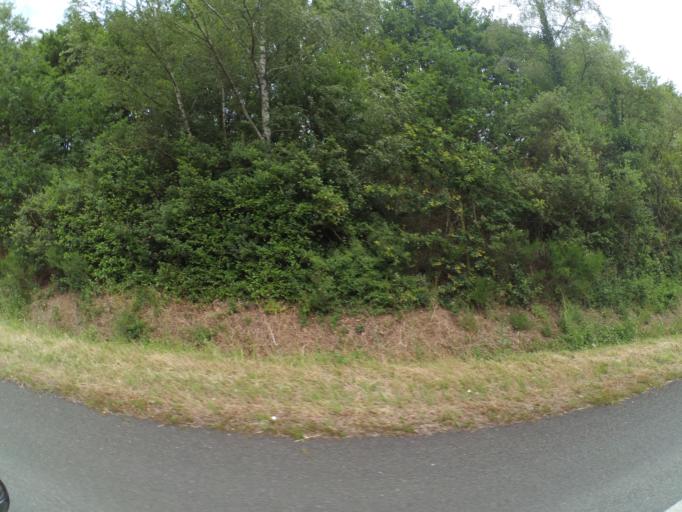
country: FR
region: Pays de la Loire
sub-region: Departement de la Vendee
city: Saint-Georges-de-Montaigu
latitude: 46.9358
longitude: -1.2981
